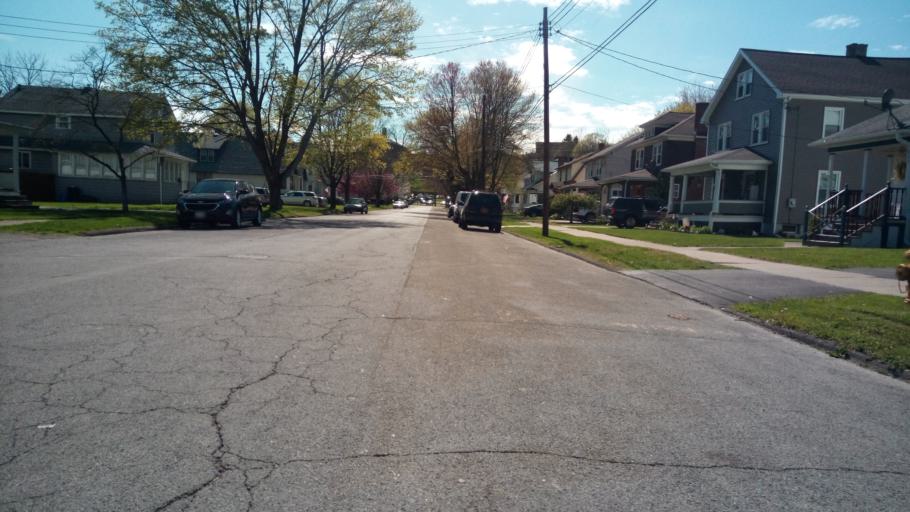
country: US
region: New York
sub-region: Chemung County
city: Elmira Heights
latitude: 42.1165
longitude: -76.8240
